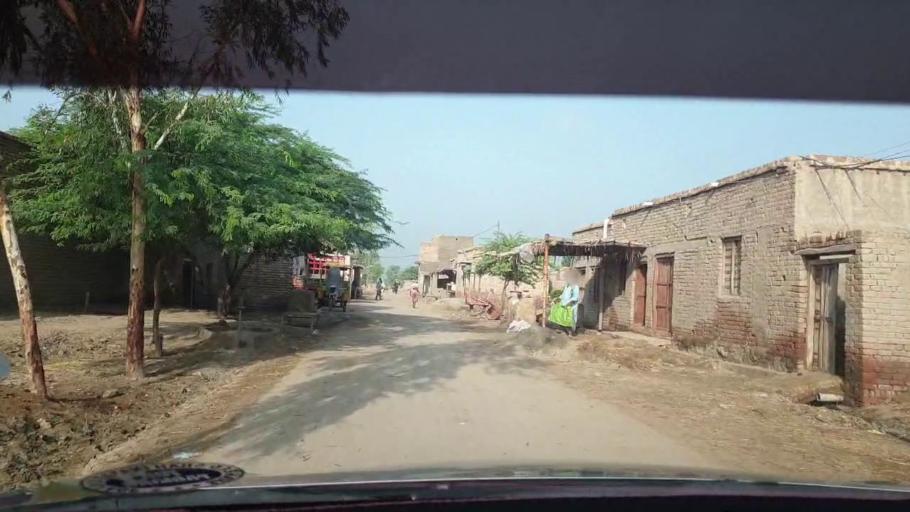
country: PK
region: Sindh
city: Goth Garelo
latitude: 27.4837
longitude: 68.0283
